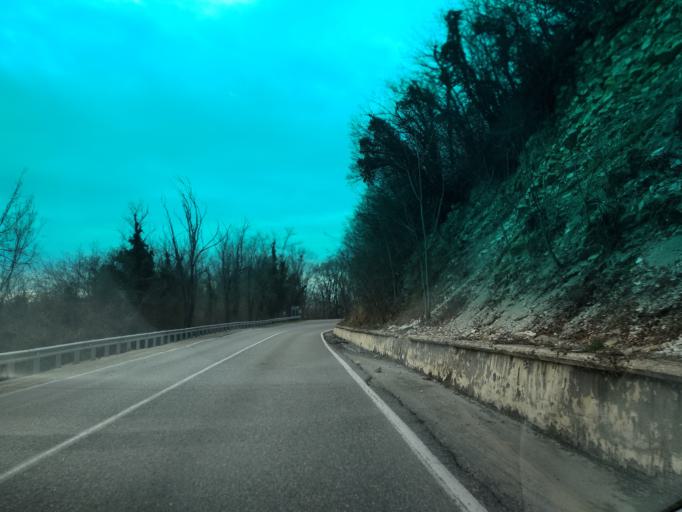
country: RU
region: Krasnodarskiy
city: Shepsi
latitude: 44.0696
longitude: 39.1375
